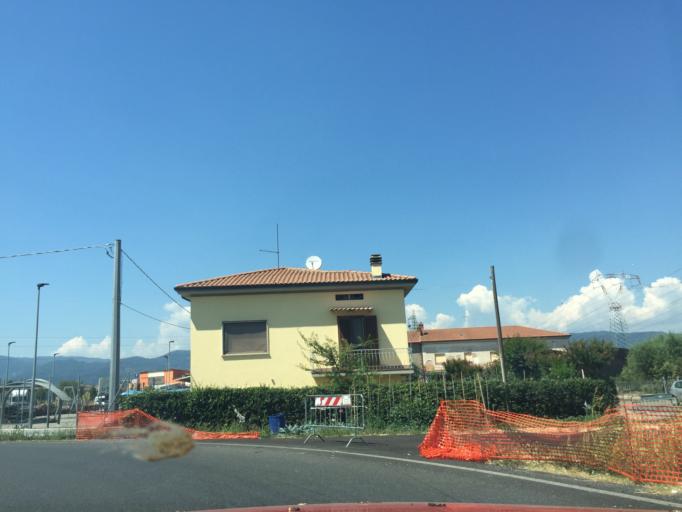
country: IT
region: Tuscany
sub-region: Provincia di Pistoia
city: Chiesina Uzzanese
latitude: 43.8461
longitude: 10.7119
